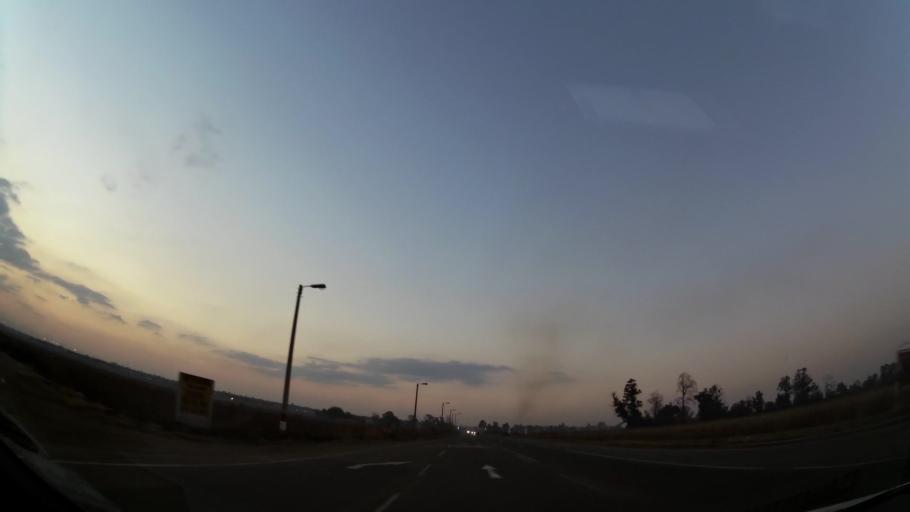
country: ZA
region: Gauteng
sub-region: Ekurhuleni Metropolitan Municipality
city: Nigel
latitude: -26.3365
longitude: 28.4546
